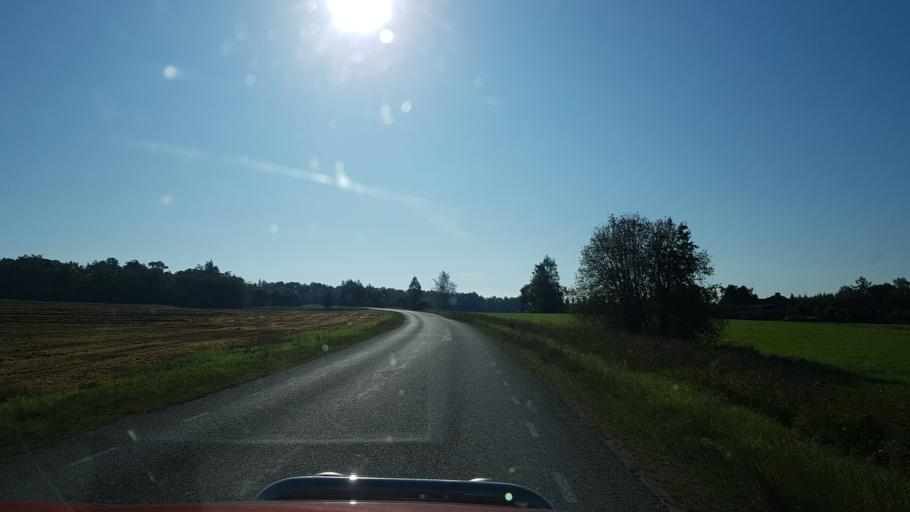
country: EE
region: Jogevamaa
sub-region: Tabivere vald
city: Tabivere
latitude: 58.6712
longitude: 26.7503
